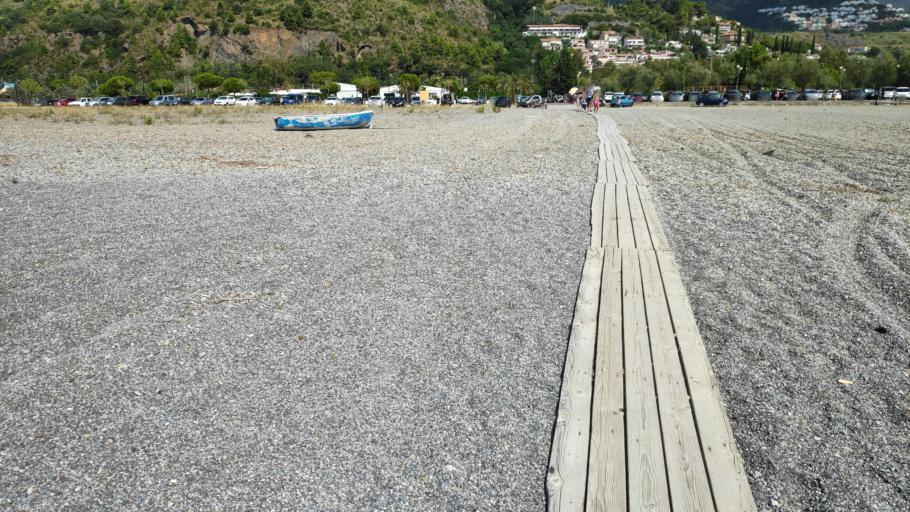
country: IT
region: Calabria
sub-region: Provincia di Cosenza
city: Praia a Mare
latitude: 39.8753
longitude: 15.7832
